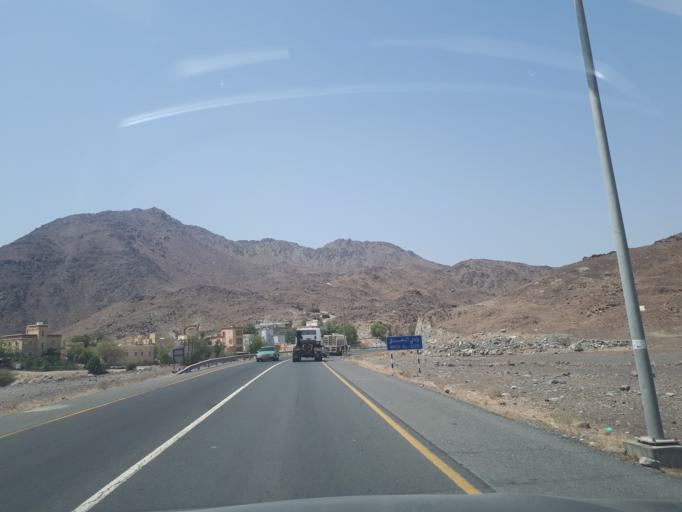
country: OM
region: Muhafazat ad Dakhiliyah
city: Sufalat Sama'il
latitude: 23.2535
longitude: 58.1014
